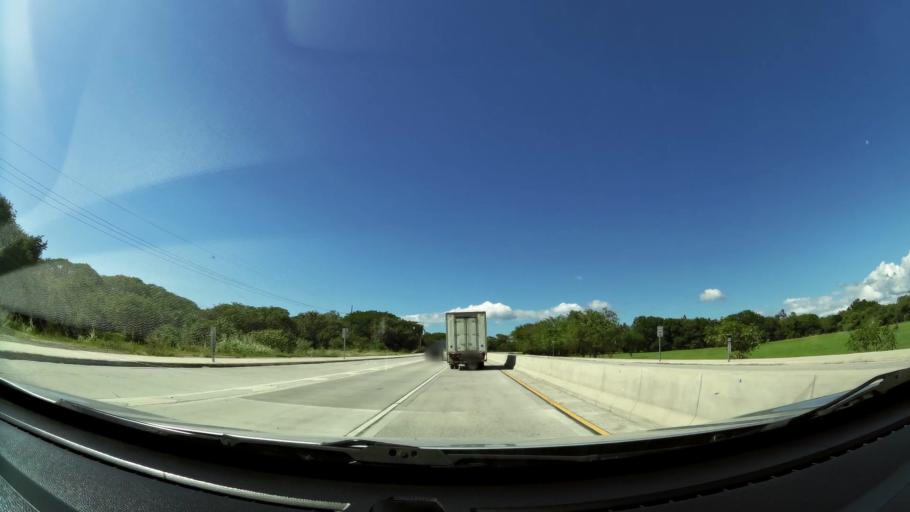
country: CR
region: Guanacaste
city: Liberia
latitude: 10.5878
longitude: -85.4174
